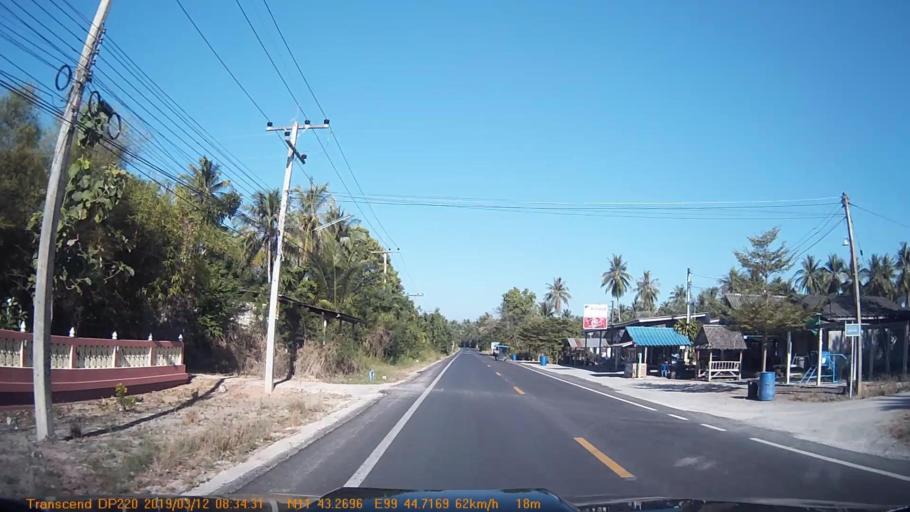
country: TH
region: Prachuap Khiri Khan
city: Prachuap Khiri Khan
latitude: 11.7213
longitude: 99.7449
